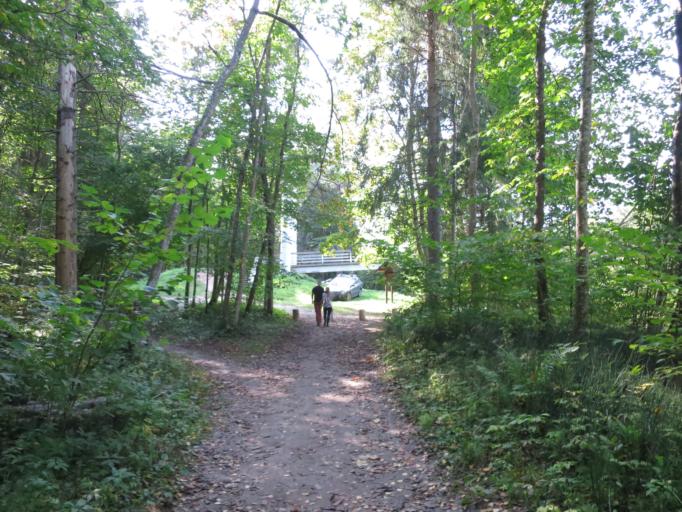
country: LV
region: Sigulda
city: Sigulda
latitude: 57.1488
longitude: 24.8083
